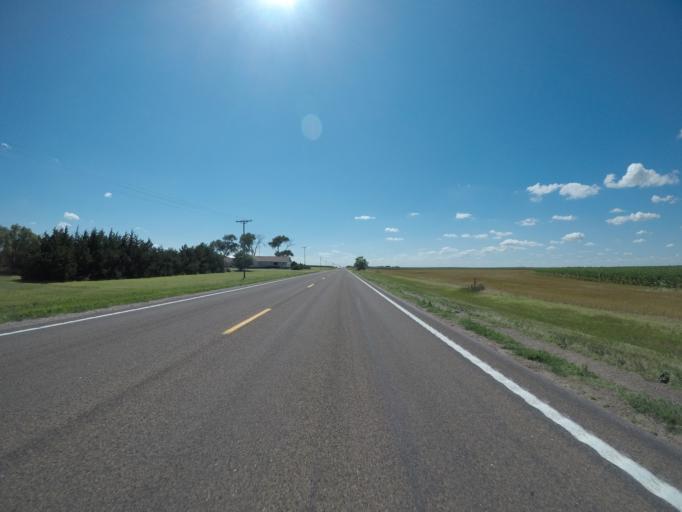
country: US
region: Nebraska
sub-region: Chase County
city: Imperial
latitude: 40.5375
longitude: -101.7858
